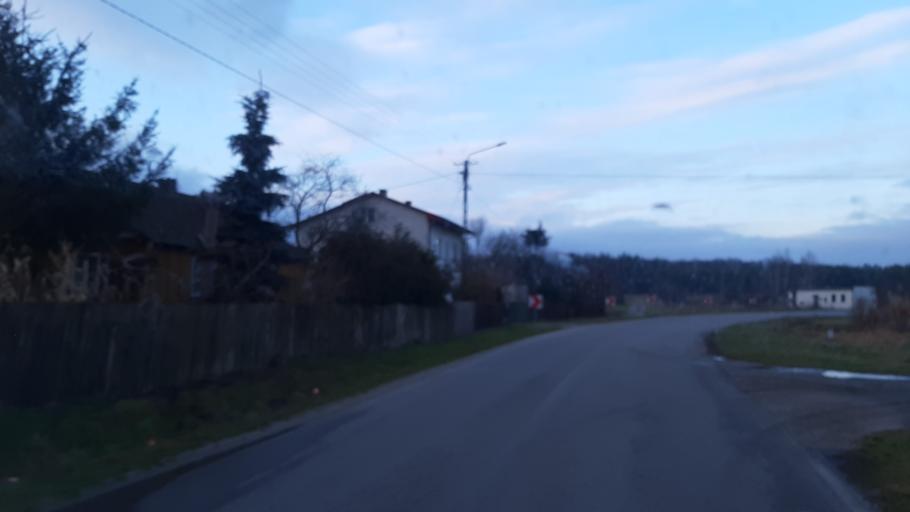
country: PL
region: Lublin Voivodeship
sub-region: Powiat lubelski
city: Garbow
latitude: 51.3938
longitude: 22.4093
